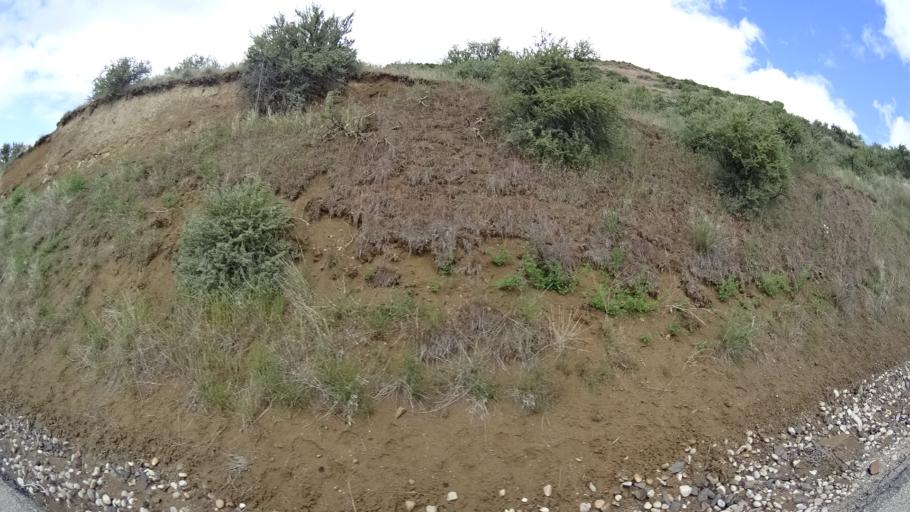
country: US
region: Idaho
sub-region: Ada County
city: Garden City
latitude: 43.7332
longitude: -116.2298
